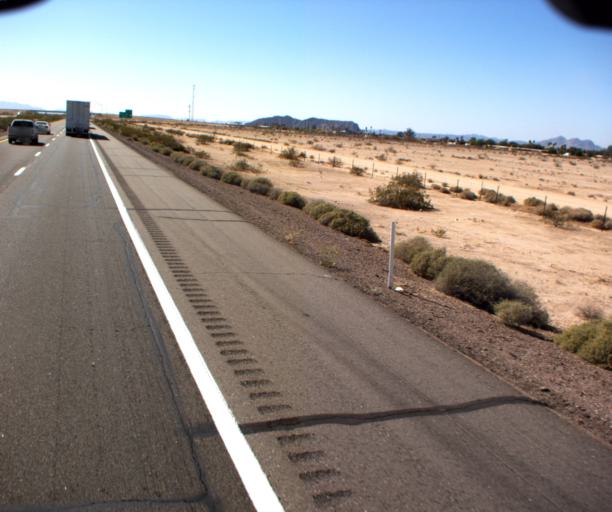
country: US
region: Arizona
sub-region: Yuma County
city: Wellton
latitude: 32.6951
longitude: -113.9442
